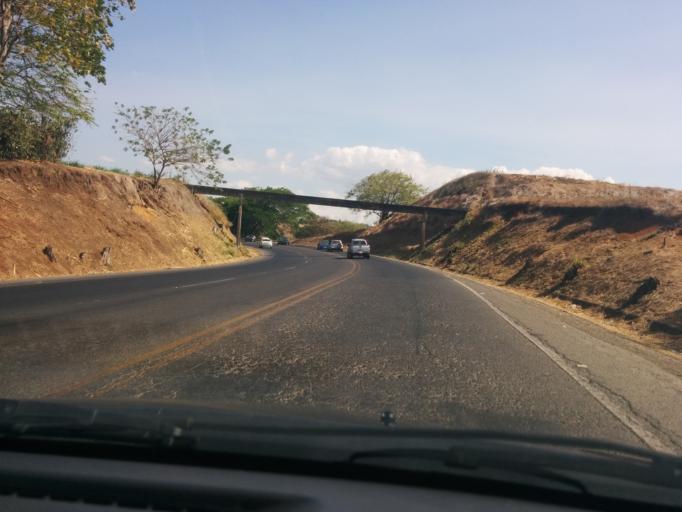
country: CR
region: Alajuela
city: Carrillos
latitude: 10.0016
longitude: -84.3179
